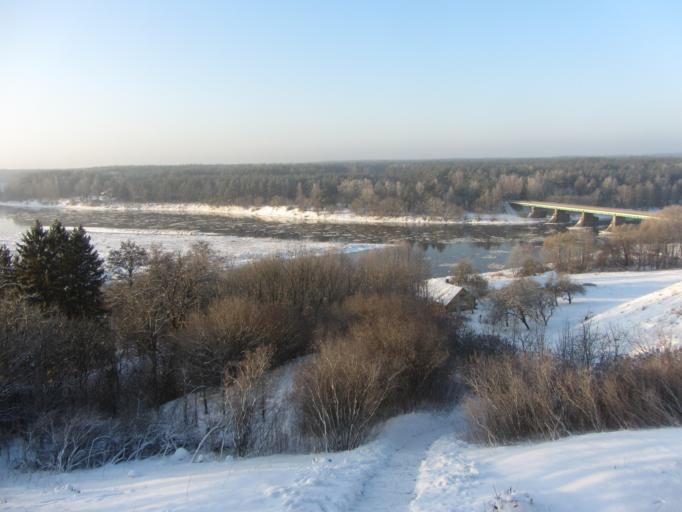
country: LT
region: Alytaus apskritis
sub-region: Alytaus rajonas
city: Daugai
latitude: 54.1581
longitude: 24.1848
